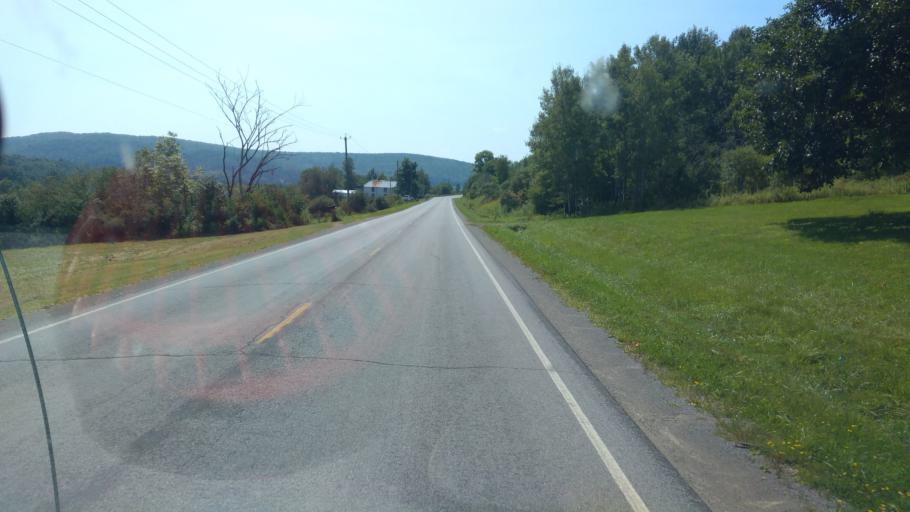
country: US
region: New York
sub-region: Allegany County
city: Belmont
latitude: 42.3153
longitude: -77.9540
